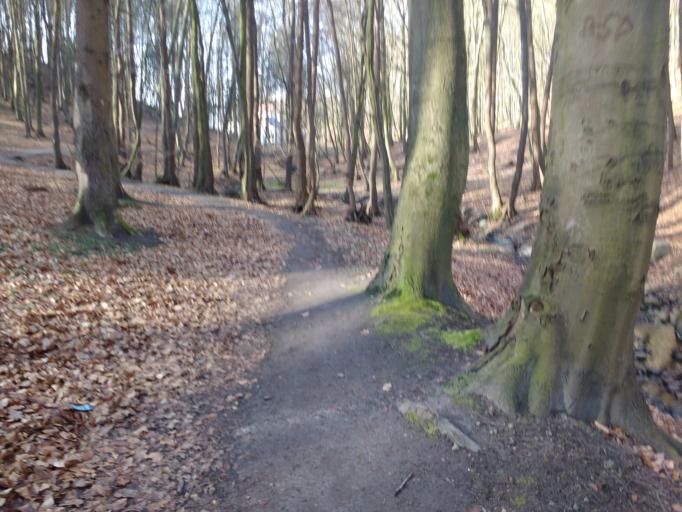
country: PL
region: Pomeranian Voivodeship
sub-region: Gdynia
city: Wielki Kack
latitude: 54.4794
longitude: 18.5141
